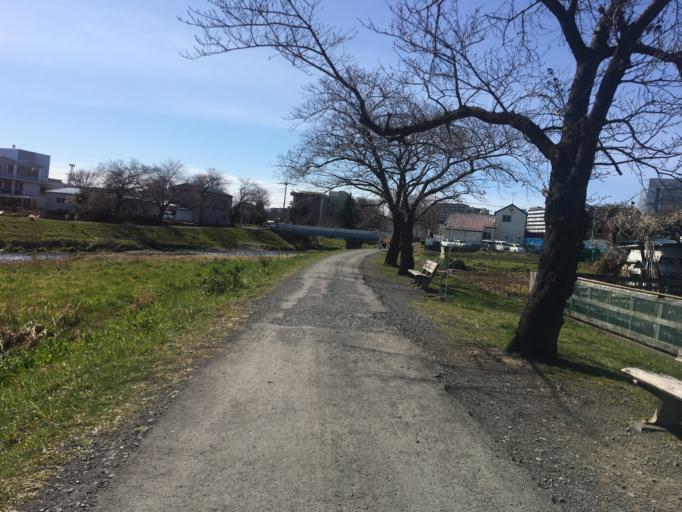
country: JP
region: Saitama
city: Asaka
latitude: 35.8092
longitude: 139.5884
